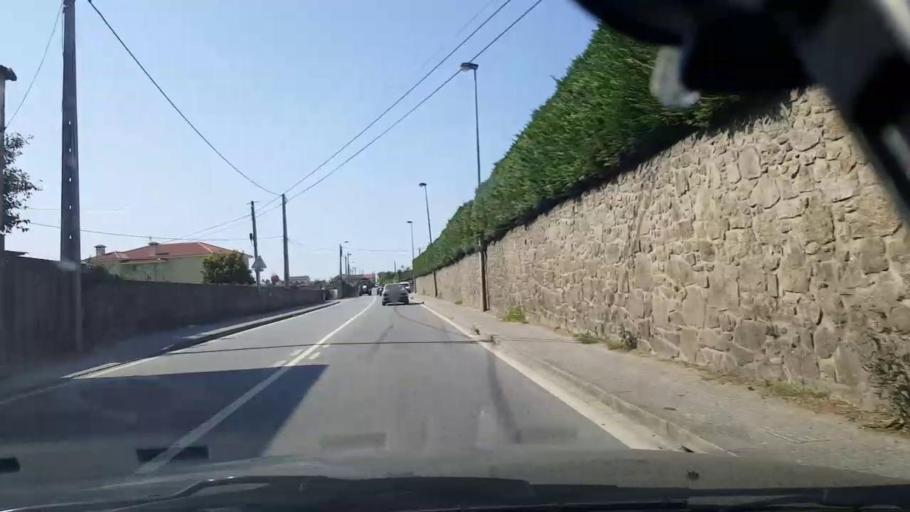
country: PT
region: Porto
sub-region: Povoa de Varzim
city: Pedroso
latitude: 41.3959
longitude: -8.6880
